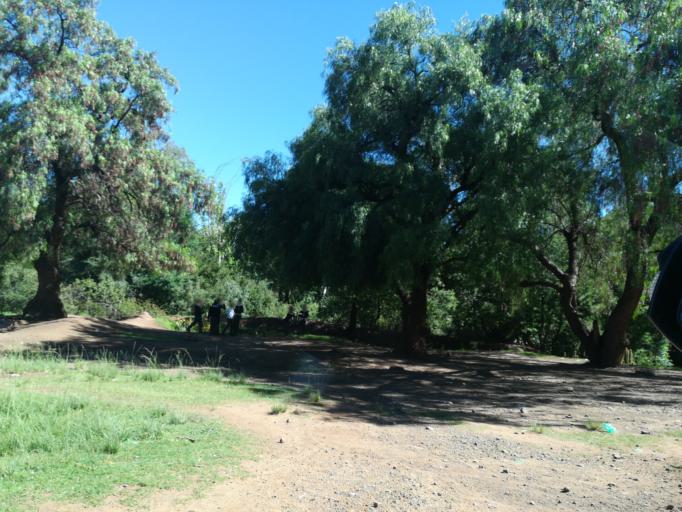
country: LS
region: Quthing
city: Quthing
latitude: -30.3418
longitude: 27.5441
